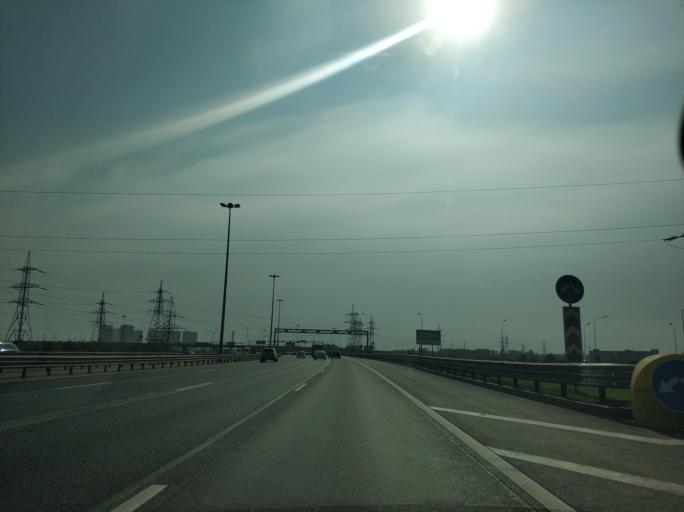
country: RU
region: Leningrad
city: Murino
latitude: 60.0214
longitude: 30.4539
